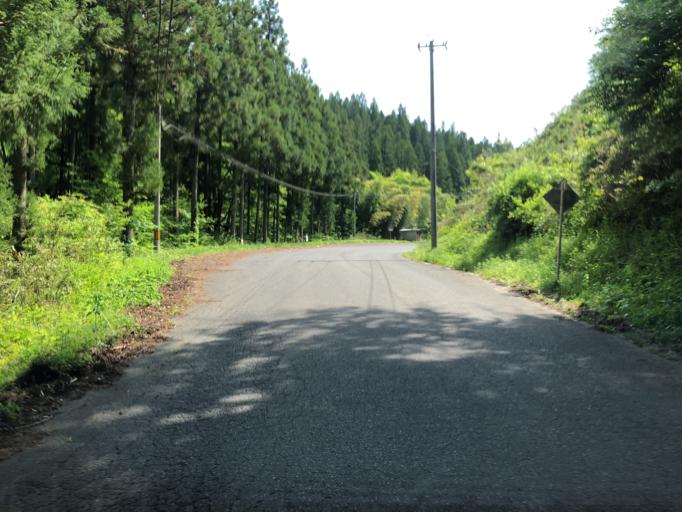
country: JP
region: Fukushima
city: Ishikawa
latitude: 37.0380
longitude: 140.5671
